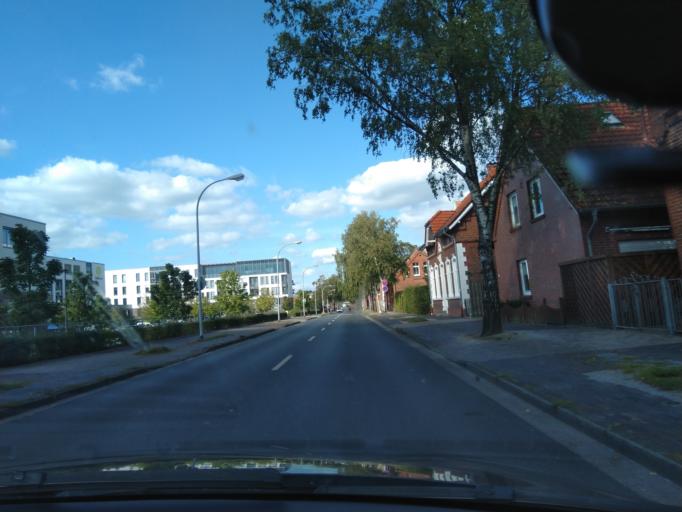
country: DE
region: Lower Saxony
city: Leer
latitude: 53.2349
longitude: 7.4596
